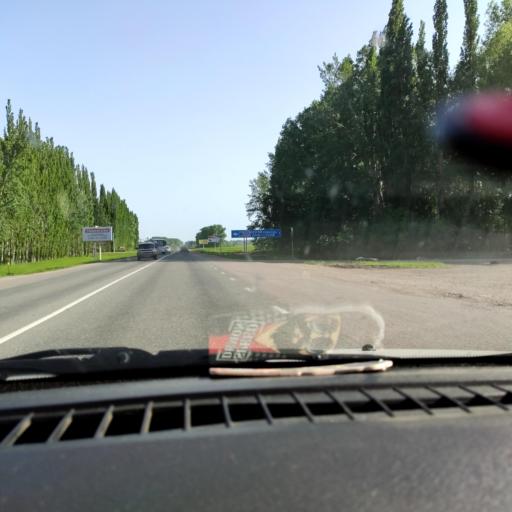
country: RU
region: Bashkortostan
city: Sterlitamak
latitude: 53.7264
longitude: 55.9438
